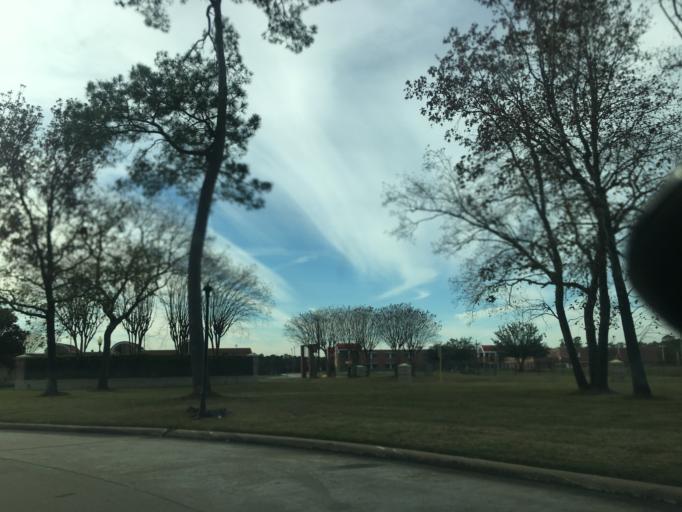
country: US
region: Texas
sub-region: Harris County
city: Cloverleaf
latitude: 29.8128
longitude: -95.1710
